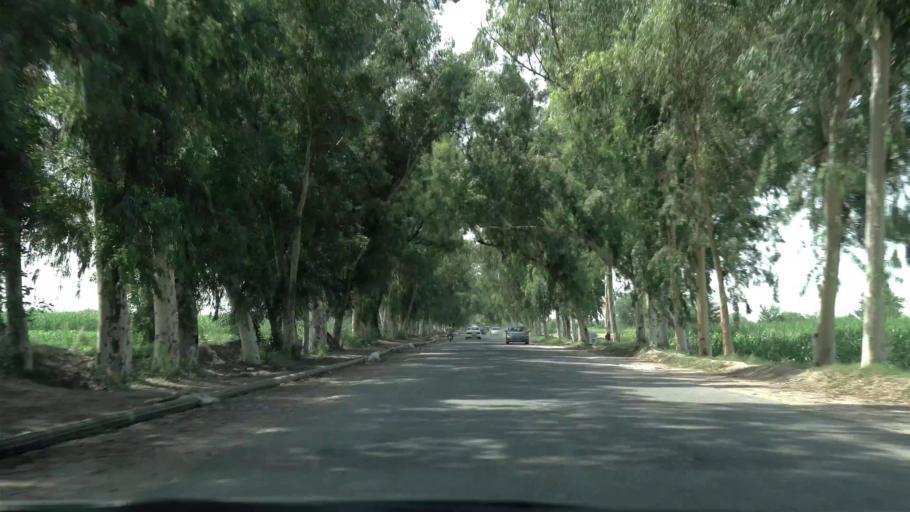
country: PK
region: Punjab
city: Gojra
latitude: 31.1729
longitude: 72.6206
